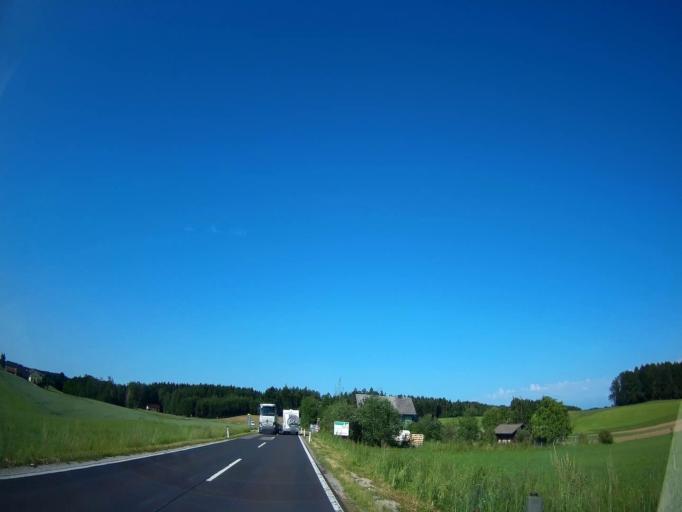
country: AT
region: Salzburg
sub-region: Politischer Bezirk Salzburg-Umgebung
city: Dorfbeuern
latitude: 48.1108
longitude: 13.0010
